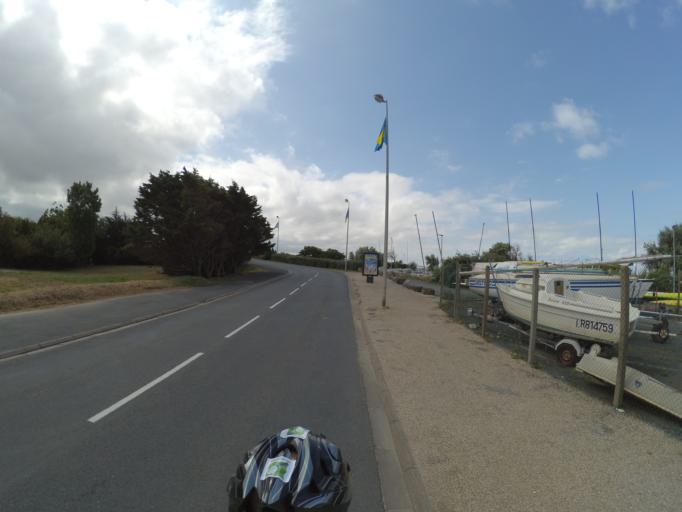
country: FR
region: Poitou-Charentes
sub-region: Departement de la Charente-Maritime
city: Chatelaillon-Plage
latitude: 46.0618
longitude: -1.0914
